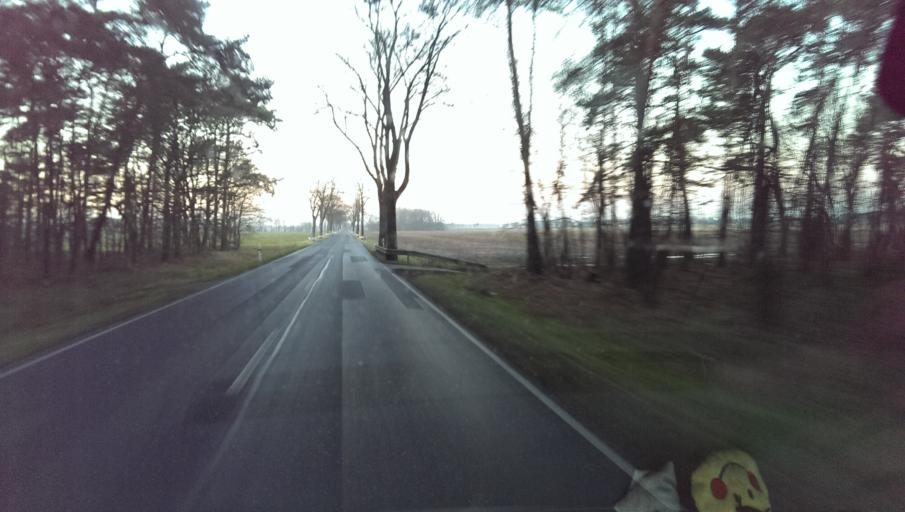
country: DE
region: Saxony-Anhalt
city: Holzdorf
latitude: 51.8062
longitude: 13.1713
